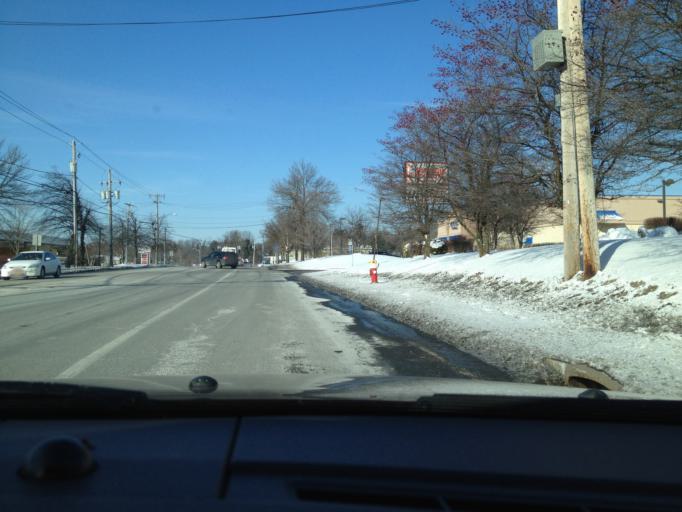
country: US
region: New York
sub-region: Albany County
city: West Albany
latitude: 42.7051
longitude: -73.7763
